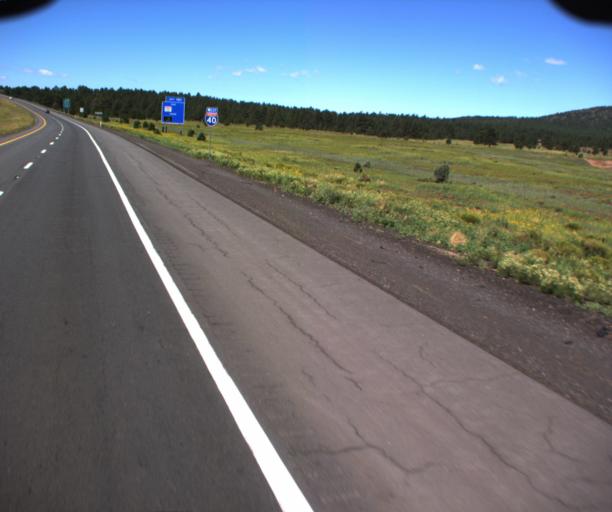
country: US
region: Arizona
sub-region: Coconino County
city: Williams
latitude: 35.2549
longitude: -112.2019
